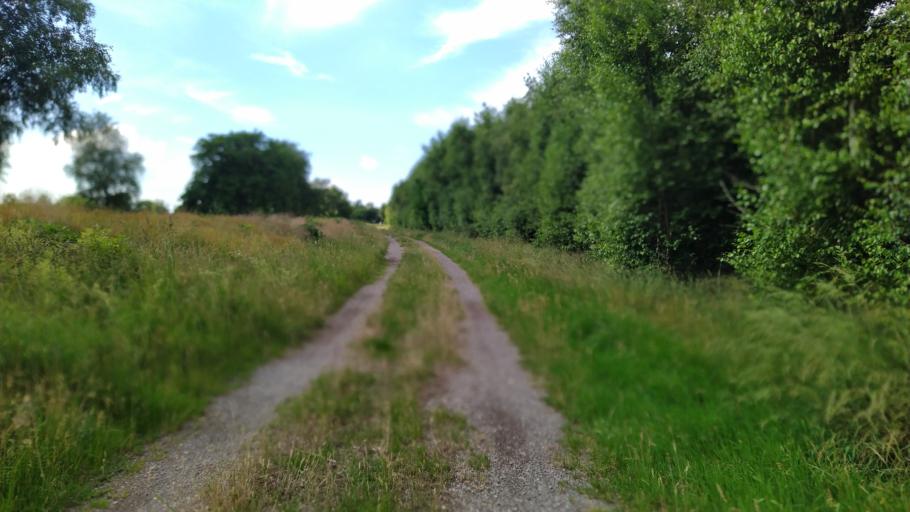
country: DE
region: Lower Saxony
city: Stinstedt
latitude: 53.6477
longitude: 8.9480
